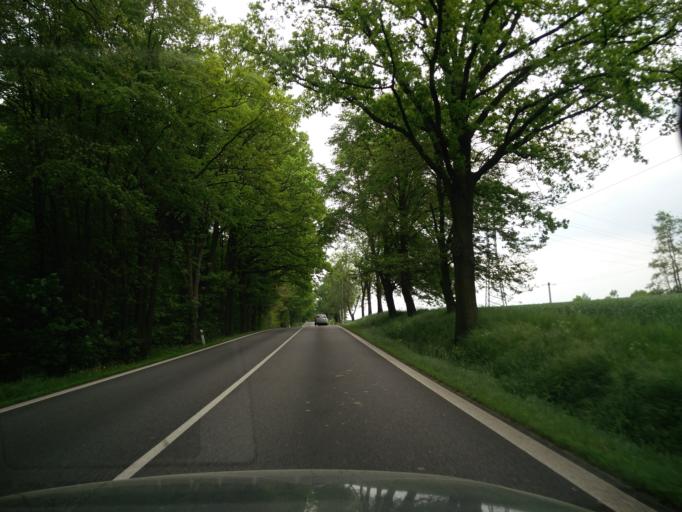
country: CZ
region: Jihocesky
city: Netolice
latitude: 49.0911
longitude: 14.2555
